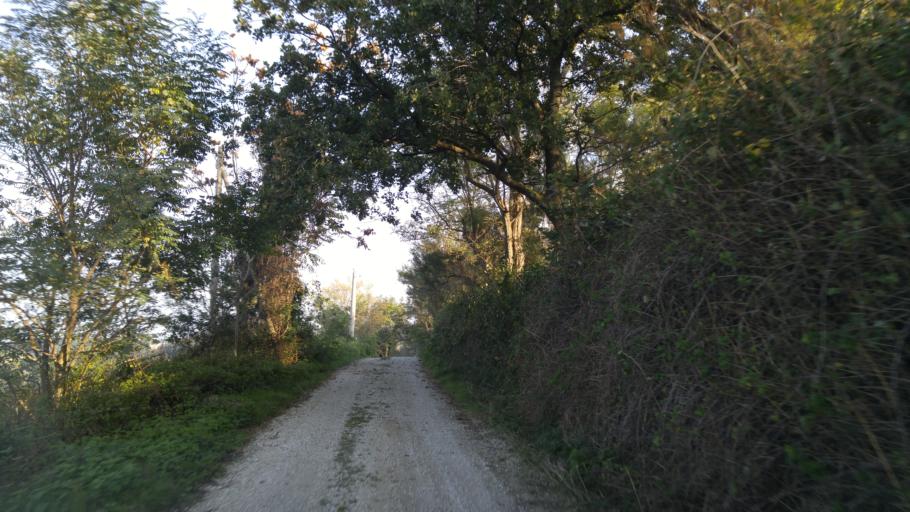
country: IT
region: The Marches
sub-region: Provincia di Pesaro e Urbino
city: Fenile
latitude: 43.8742
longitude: 12.9604
